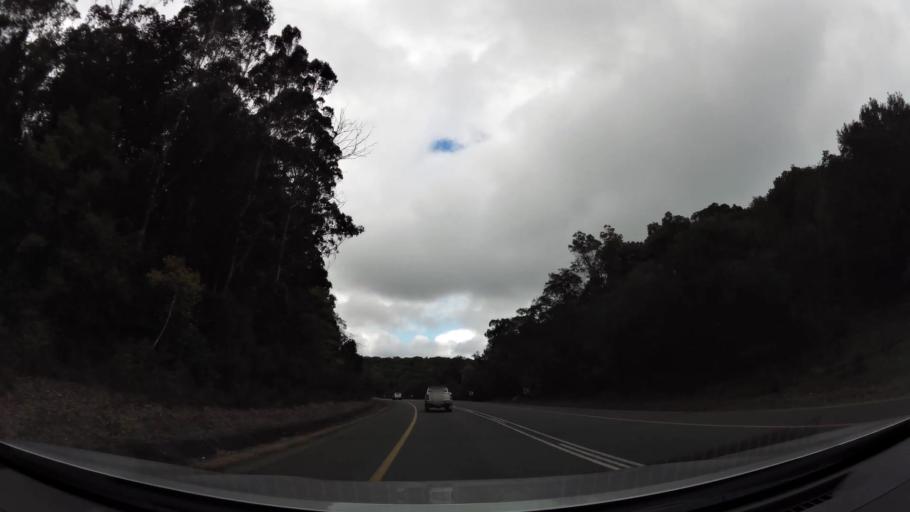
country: ZA
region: Western Cape
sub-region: Eden District Municipality
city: Knysna
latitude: -34.0366
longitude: 23.2037
